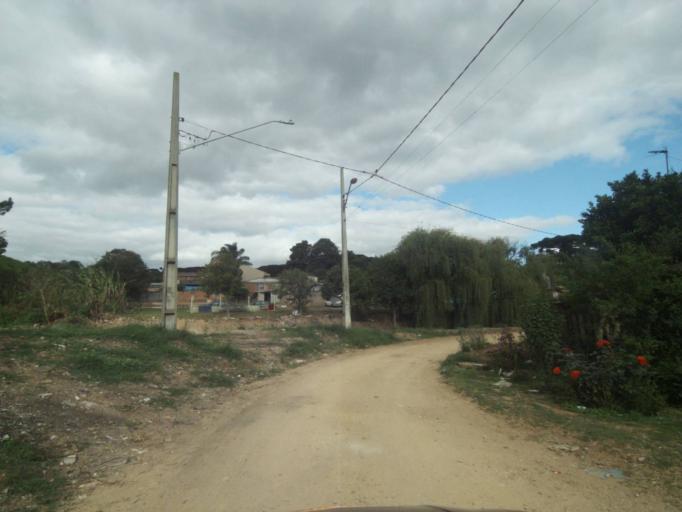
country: BR
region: Parana
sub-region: Sao Jose Dos Pinhais
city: Sao Jose dos Pinhais
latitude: -25.5474
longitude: -49.2461
